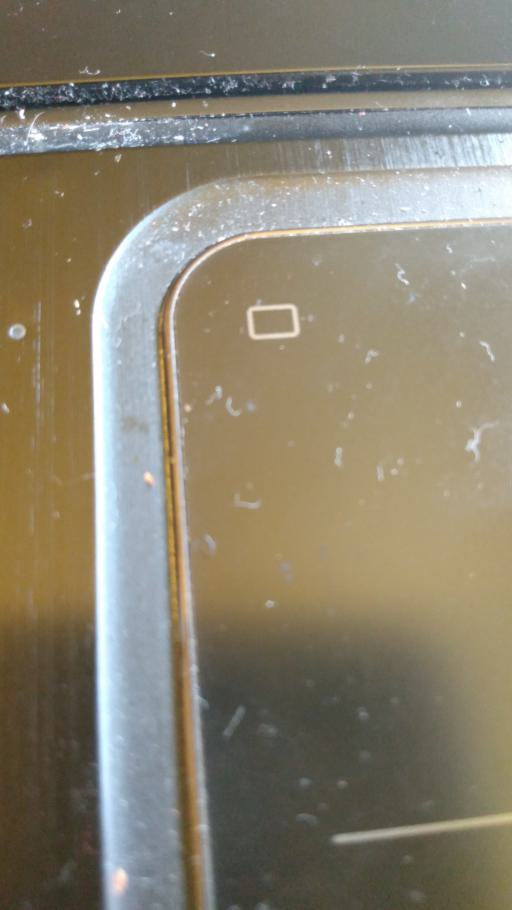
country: RU
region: Moskovskaya
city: Kolomna
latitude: 55.0492
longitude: 38.9010
